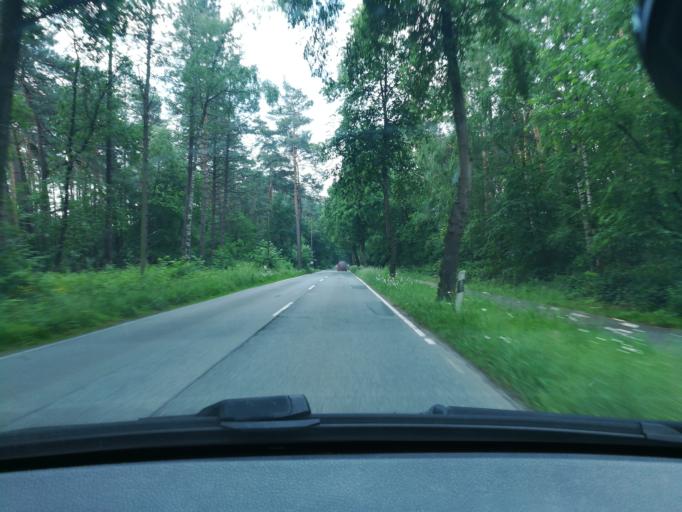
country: DE
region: North Rhine-Westphalia
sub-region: Regierungsbezirk Detmold
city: Oerlinghausen
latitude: 51.9185
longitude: 8.6555
